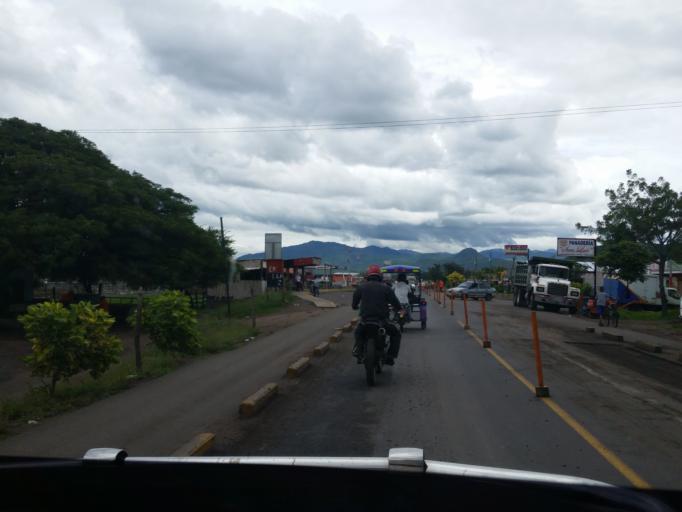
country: NI
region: Matagalpa
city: Ciudad Dario
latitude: 12.8584
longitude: -86.0959
